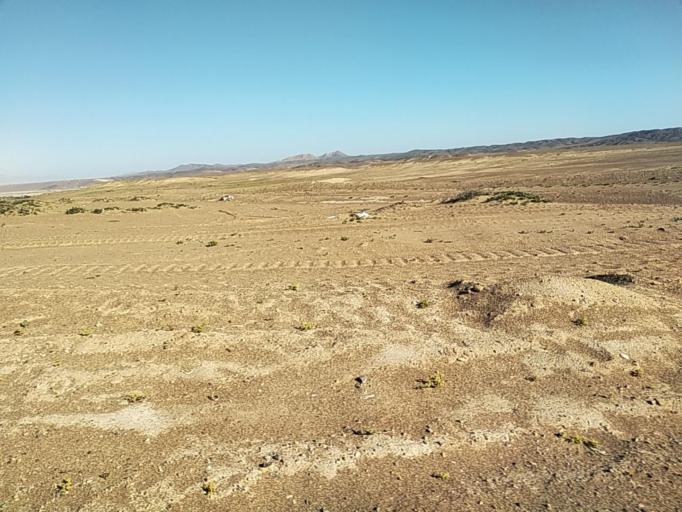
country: CL
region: Atacama
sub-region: Provincia de Copiapo
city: Copiapo
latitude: -27.3308
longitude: -70.7858
